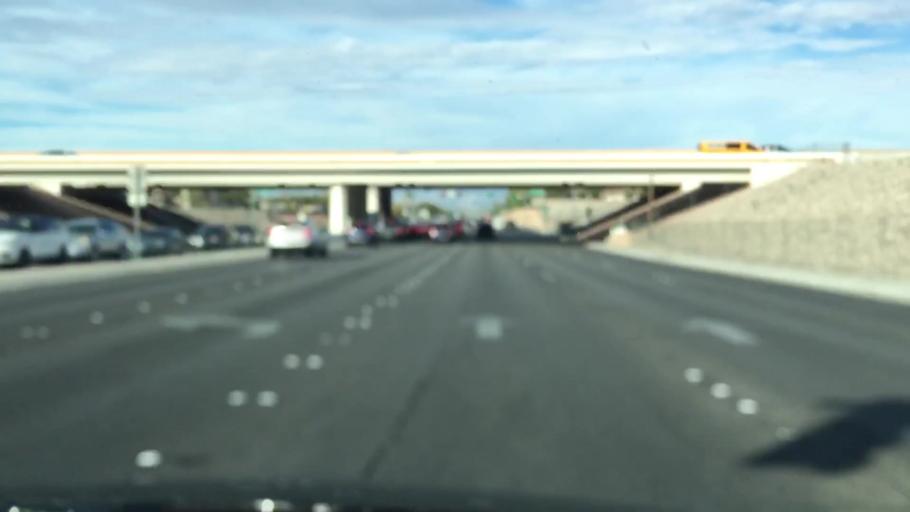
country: US
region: Nevada
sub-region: Clark County
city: Whitney
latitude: 36.0228
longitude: -115.1005
